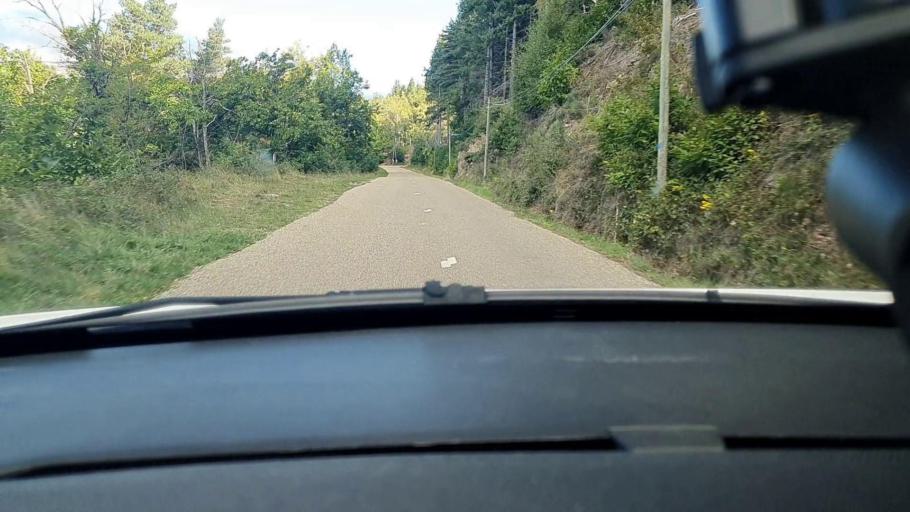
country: FR
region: Rhone-Alpes
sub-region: Departement de l'Ardeche
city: Les Vans
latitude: 44.4243
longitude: 4.0235
